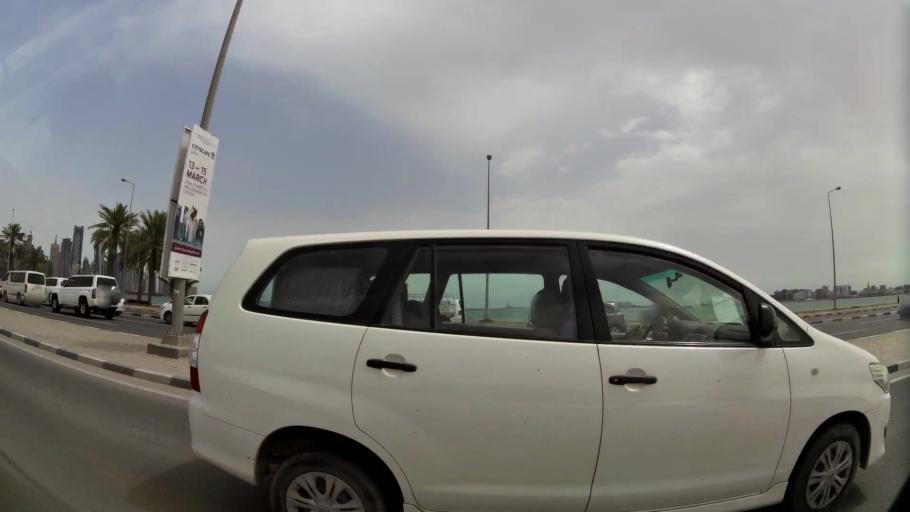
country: QA
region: Baladiyat ad Dawhah
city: Doha
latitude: 25.3028
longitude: 51.5179
